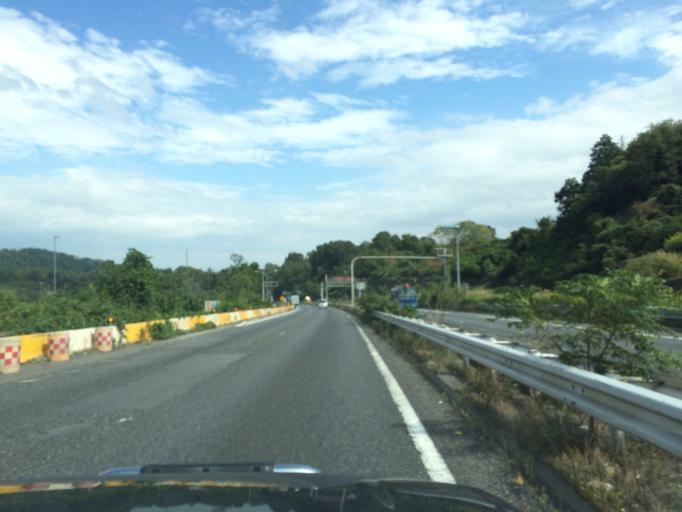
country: JP
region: Mie
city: Nabari
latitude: 34.6948
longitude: 136.0590
